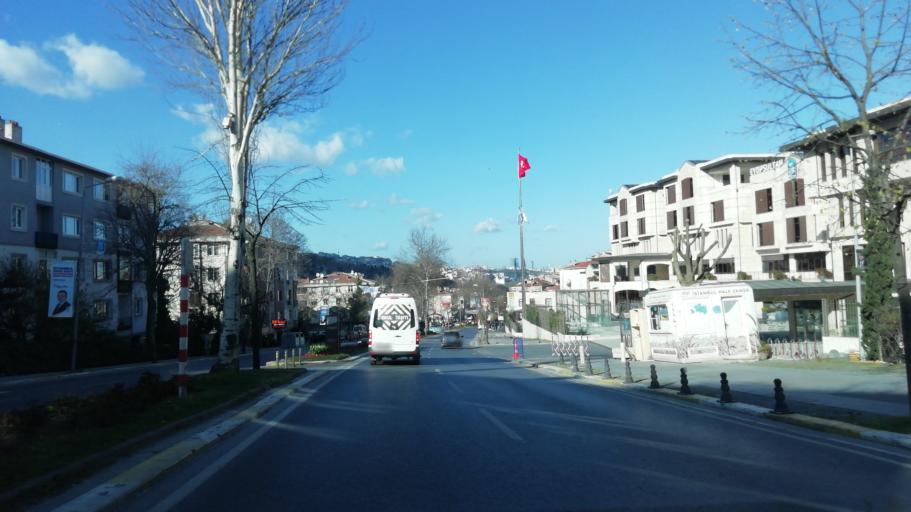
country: TR
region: Istanbul
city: Istanbul
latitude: 41.0427
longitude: 28.9286
